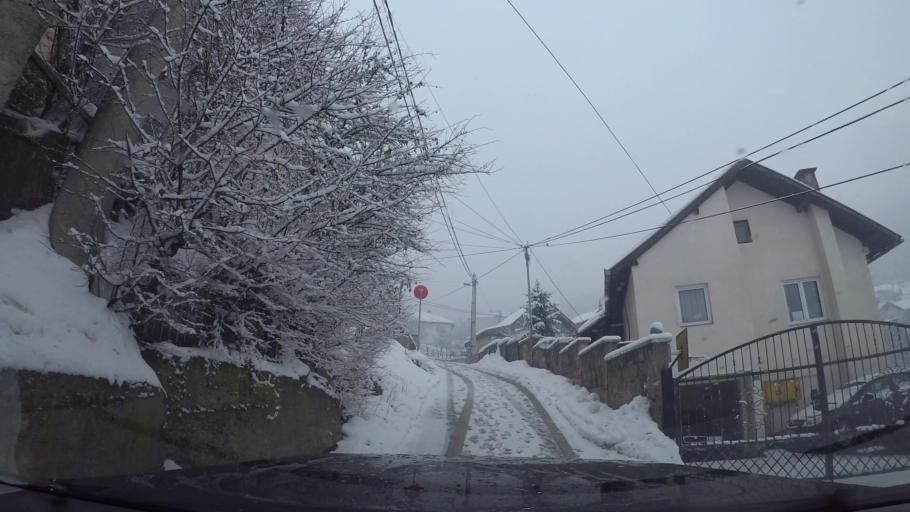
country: BA
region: Federation of Bosnia and Herzegovina
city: Kobilja Glava
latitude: 43.8464
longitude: 18.4279
